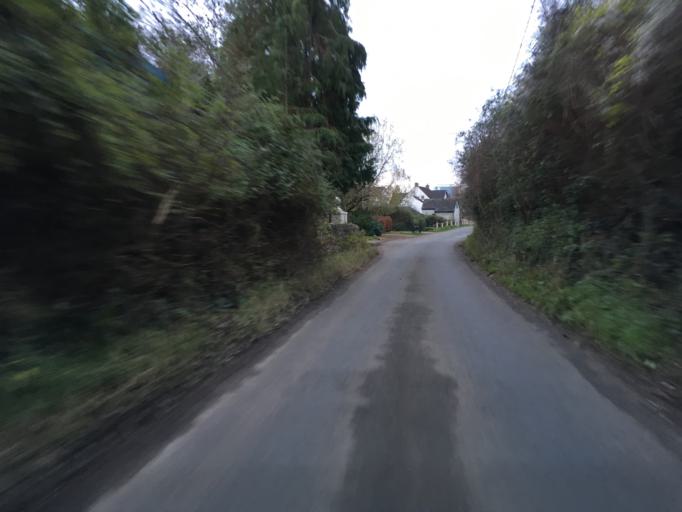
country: GB
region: Wales
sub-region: Newport
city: Bishton
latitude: 51.5858
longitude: -2.8779
